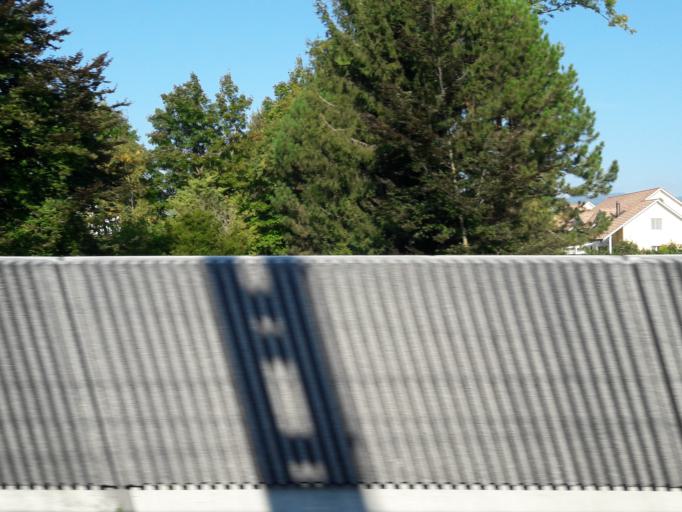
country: CH
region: Vaud
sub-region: Nyon District
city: Prangins
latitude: 46.3973
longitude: 6.2465
